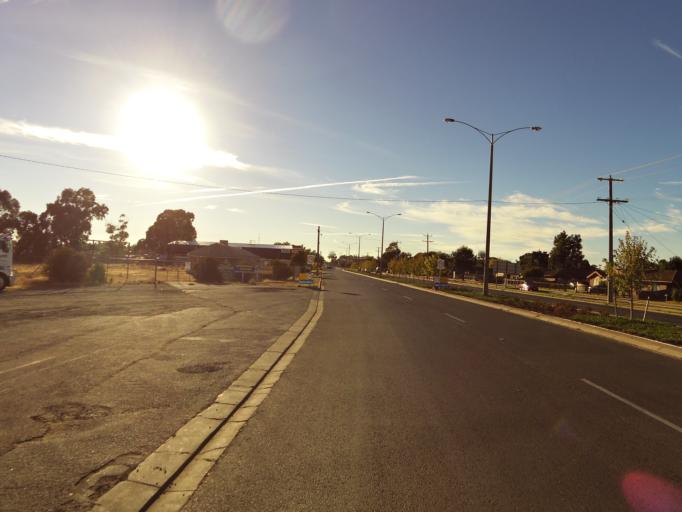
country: AU
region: Victoria
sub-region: Campaspe
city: Echuca
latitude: -36.1405
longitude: 144.7306
